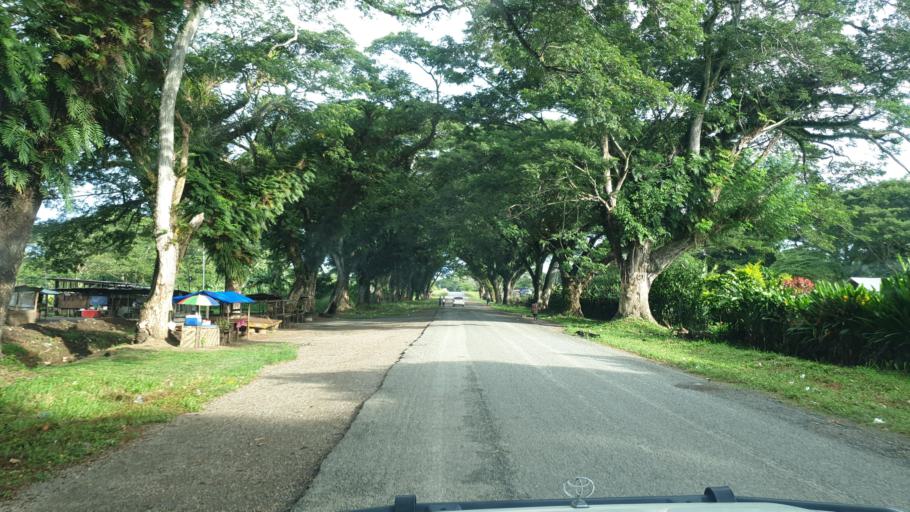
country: PG
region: National Capital
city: Port Moresby
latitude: -9.2026
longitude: 147.2372
